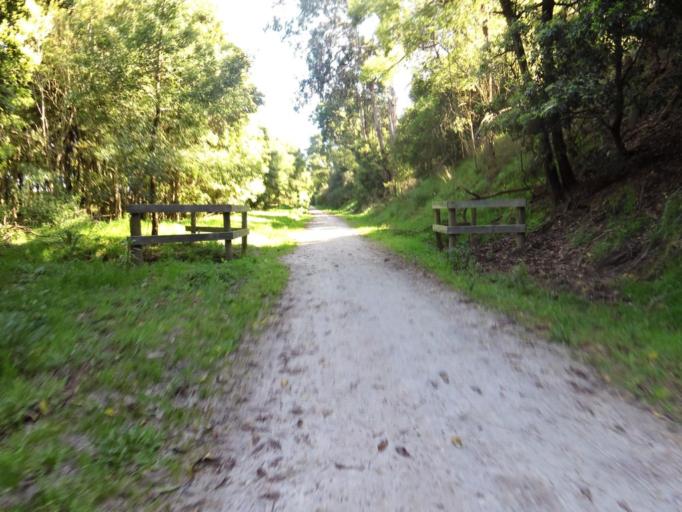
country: AU
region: Victoria
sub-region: Latrobe
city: Morwell
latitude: -38.6755
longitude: 146.1628
